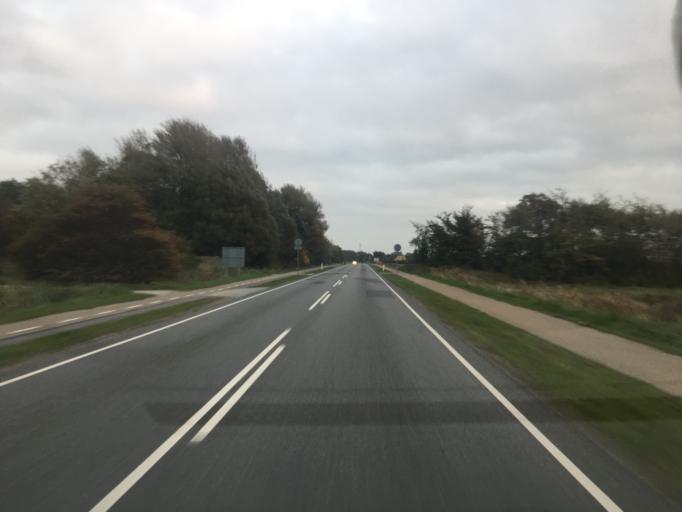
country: DK
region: South Denmark
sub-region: Tonder Kommune
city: Tonder
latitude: 54.9473
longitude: 8.8369
